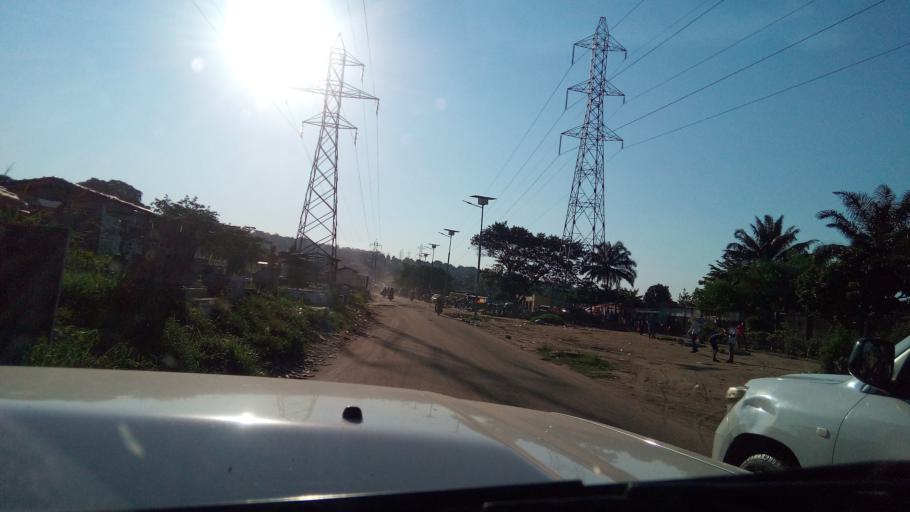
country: CD
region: Kinshasa
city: Kinshasa
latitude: -4.3579
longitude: 15.2671
